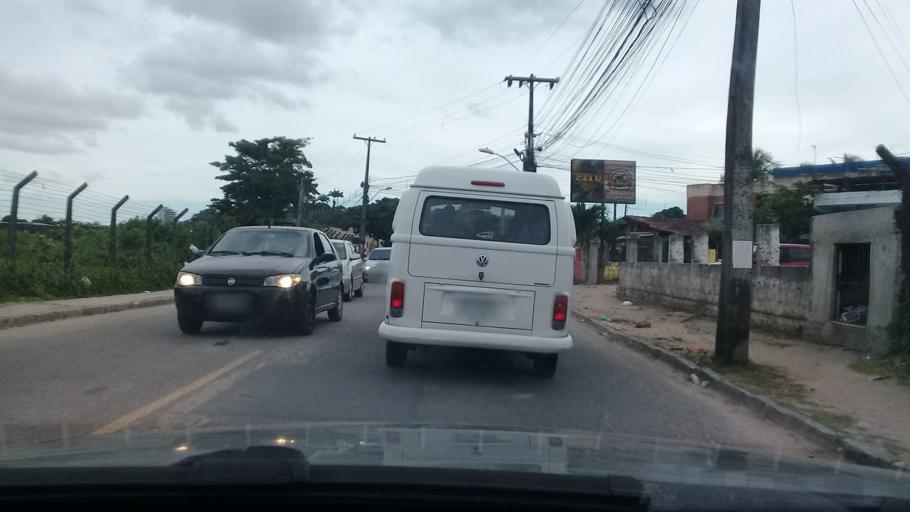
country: BR
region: Pernambuco
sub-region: Sao Lourenco Da Mata
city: Sao Lourenco da Mata
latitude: -8.0303
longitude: -34.9582
